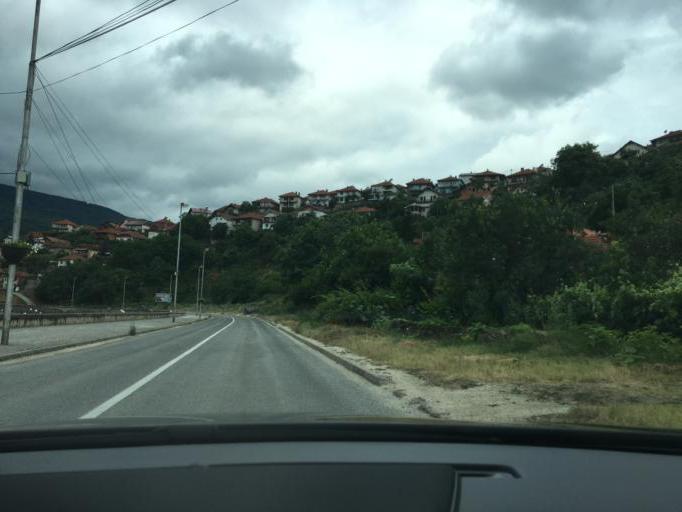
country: MK
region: Kriva Palanka
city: Kriva Palanka
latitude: 42.2061
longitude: 22.3340
